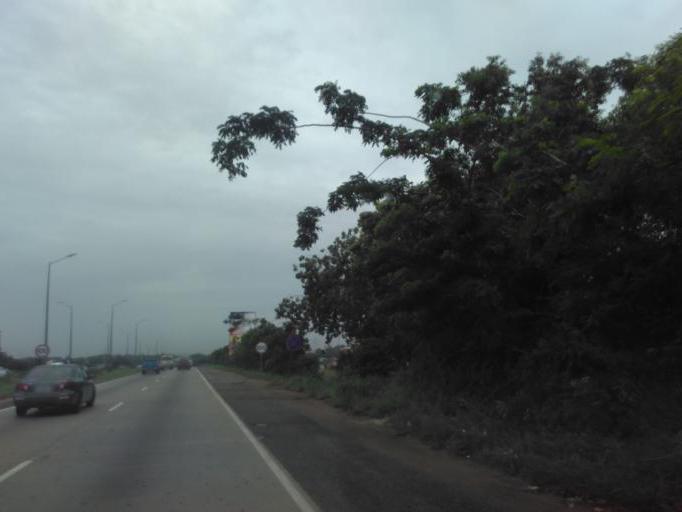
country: GH
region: Greater Accra
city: Medina Estates
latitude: 5.6263
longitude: -0.1660
